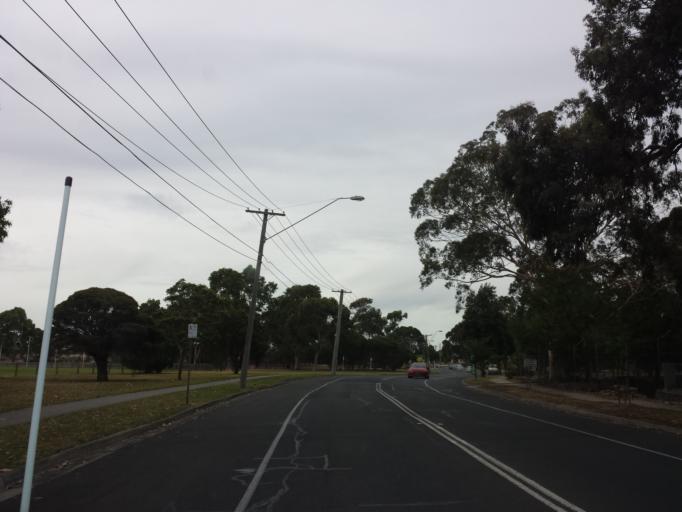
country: AU
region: Victoria
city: Highett
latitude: -37.9426
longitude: 145.0522
